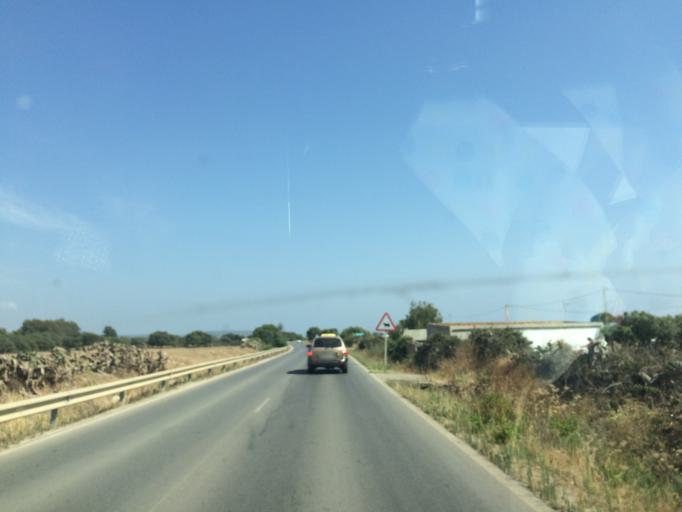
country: ES
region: Andalusia
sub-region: Provincia de Cadiz
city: Conil de la Frontera
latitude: 36.2489
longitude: -6.0668
